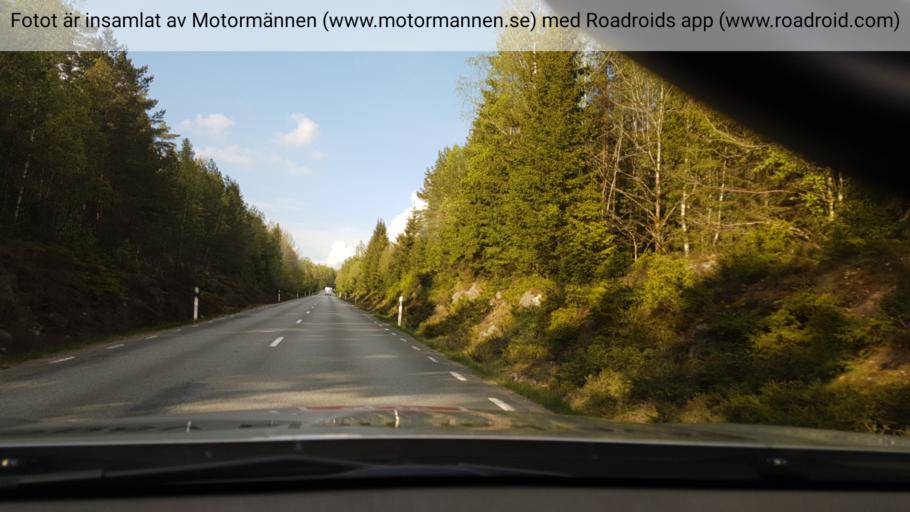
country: SE
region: Joenkoeping
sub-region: Vaggeryds Kommun
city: Skillingaryd
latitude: 57.3910
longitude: 14.0175
